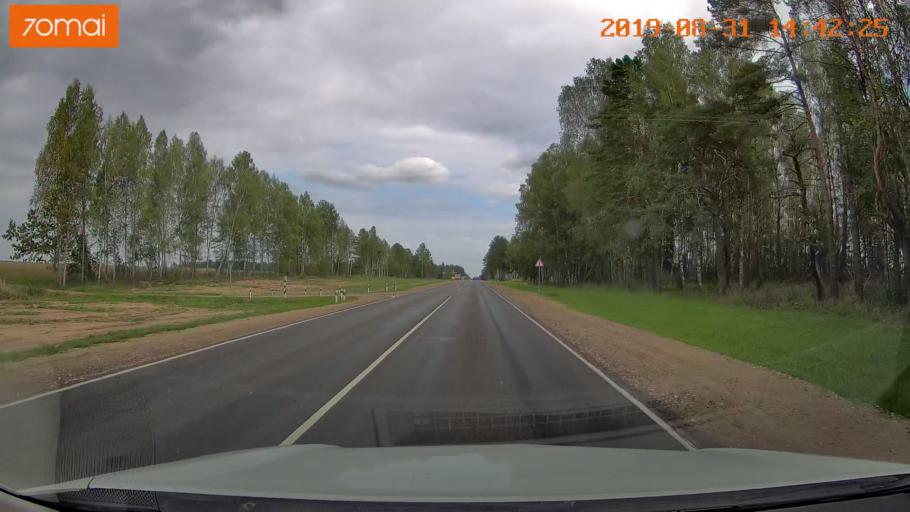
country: RU
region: Smolensk
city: Yekimovichi
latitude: 54.2079
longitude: 33.6077
